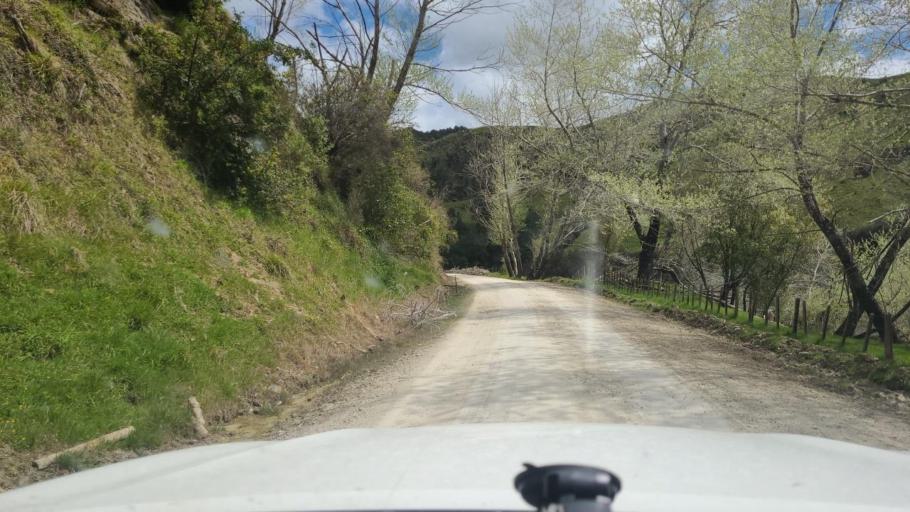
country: NZ
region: Gisborne
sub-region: Gisborne District
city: Gisborne
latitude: -38.8295
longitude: 177.7263
